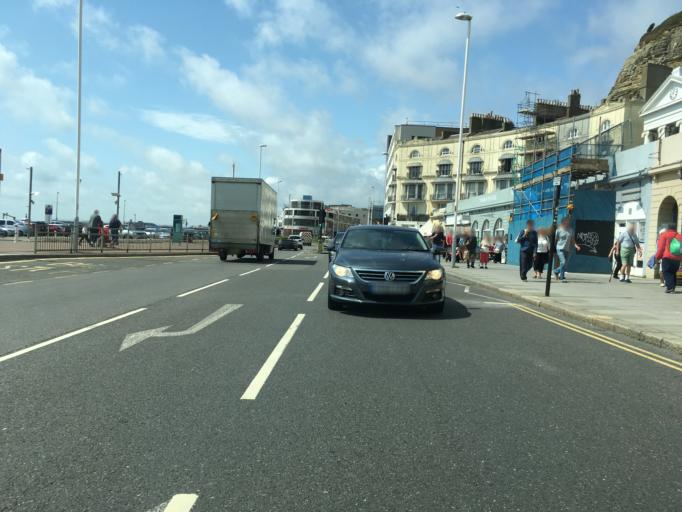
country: GB
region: England
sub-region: East Sussex
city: Hastings
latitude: 50.8553
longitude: 0.5855
